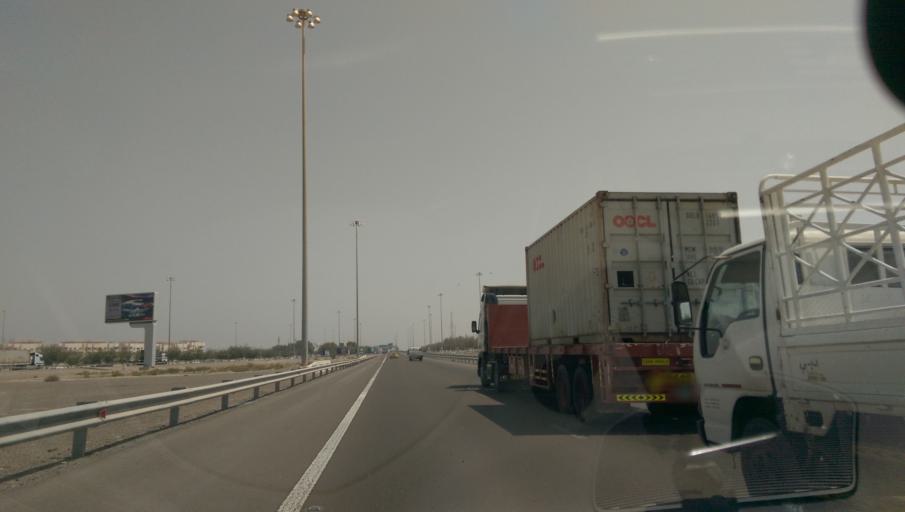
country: AE
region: Abu Dhabi
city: Abu Dhabi
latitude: 24.5455
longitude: 54.6940
